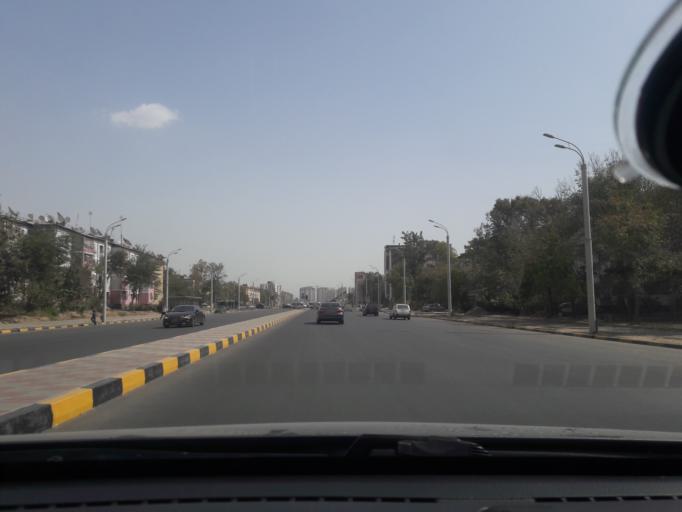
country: TJ
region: Dushanbe
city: Dushanbe
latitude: 38.5585
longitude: 68.7456
